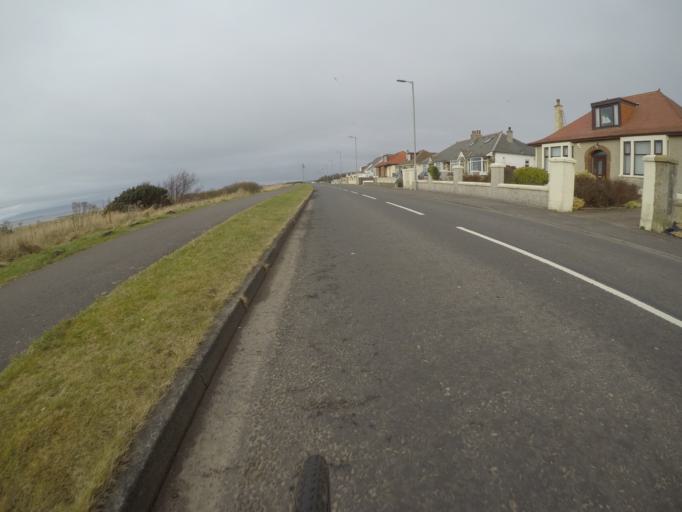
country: GB
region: Scotland
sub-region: North Ayrshire
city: Ardrossan
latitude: 55.6498
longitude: -4.8161
